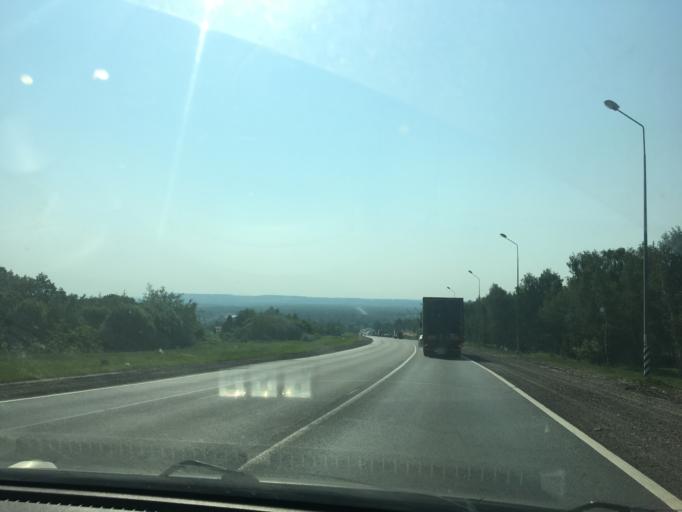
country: RU
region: Nizjnij Novgorod
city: Kstovo
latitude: 56.1057
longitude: 44.2901
